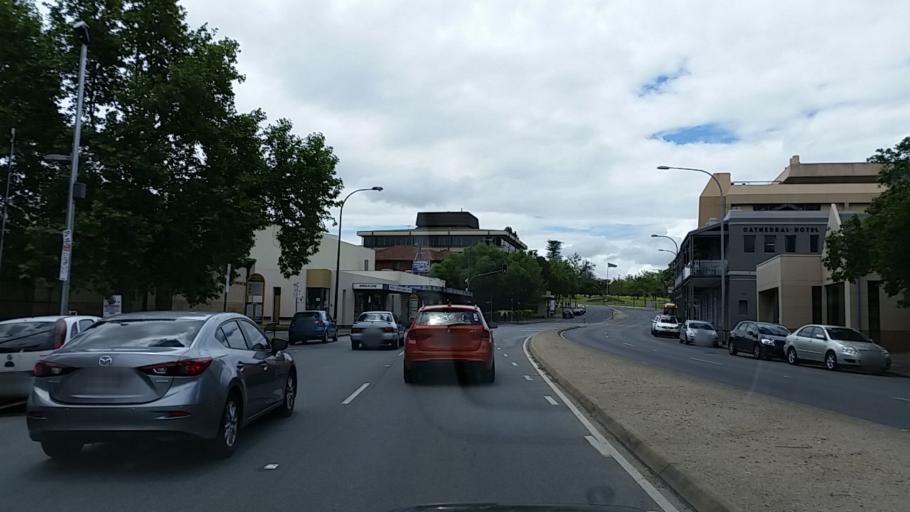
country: AU
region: South Australia
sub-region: Adelaide
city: North Adelaide
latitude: -34.9128
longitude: 138.5987
